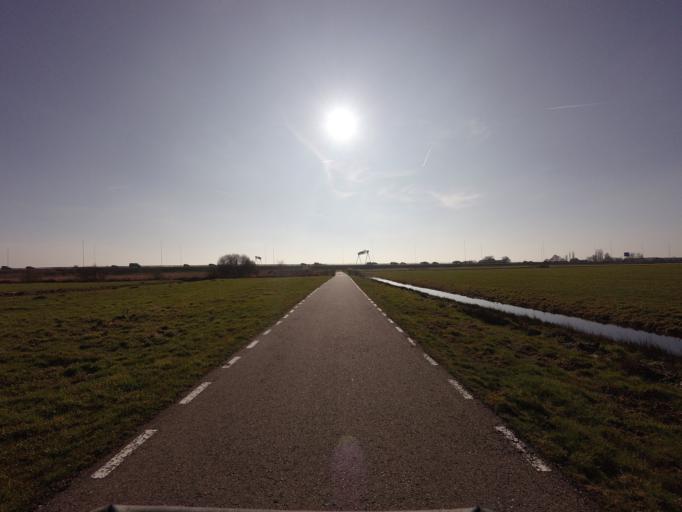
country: NL
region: South Holland
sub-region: Bodegraven-Reeuwijk
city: Bodegraven
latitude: 52.0677
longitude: 4.7806
